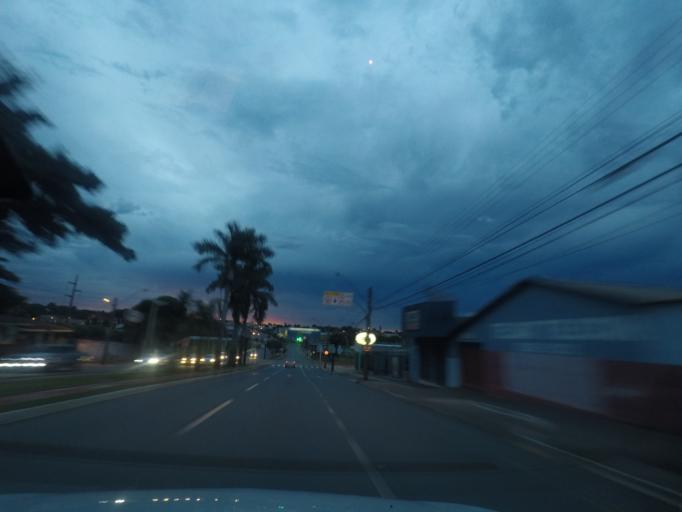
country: BR
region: Goias
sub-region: Goiania
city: Goiania
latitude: -16.7175
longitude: -49.2928
